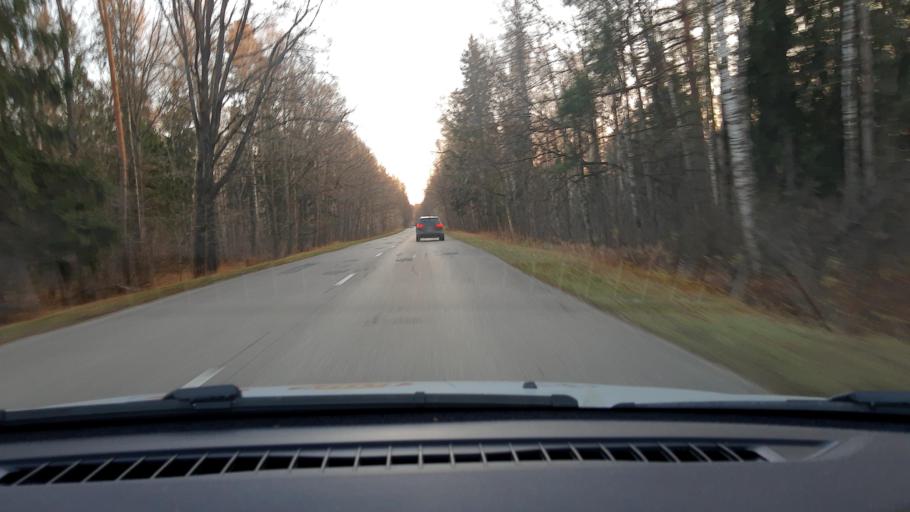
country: RU
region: Nizjnij Novgorod
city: Volodarsk
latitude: 56.2650
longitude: 43.1681
